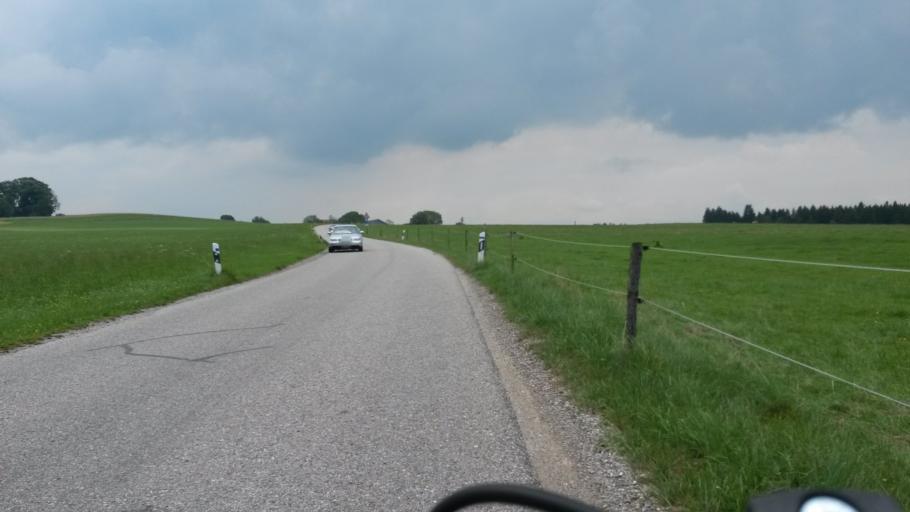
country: DE
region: Bavaria
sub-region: Upper Bavaria
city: Hoslwang
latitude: 47.9688
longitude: 12.3162
